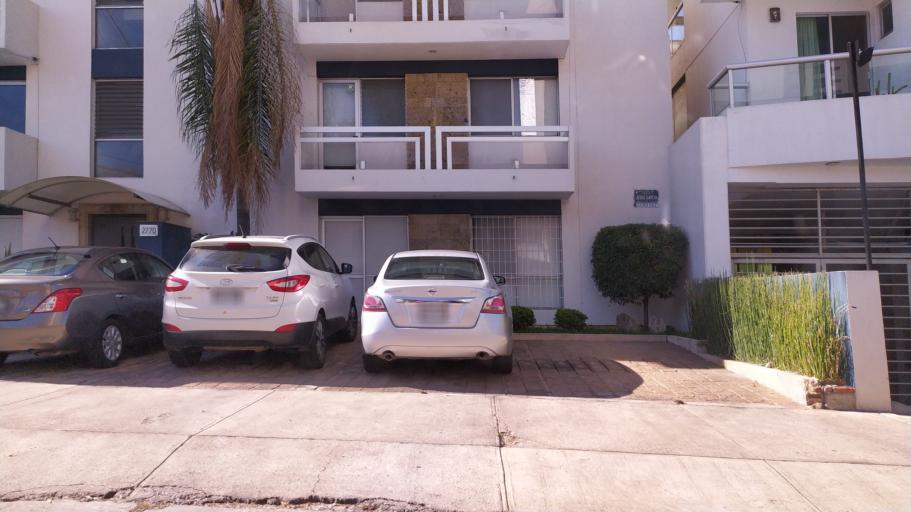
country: MX
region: Jalisco
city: Guadalajara
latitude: 20.6895
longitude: -103.3855
